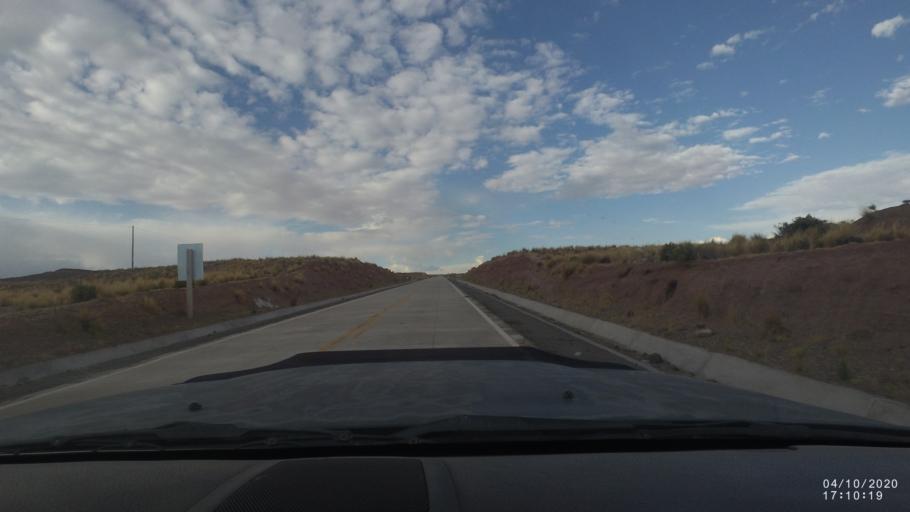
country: BO
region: Oruro
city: Oruro
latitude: -18.3325
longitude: -67.5850
